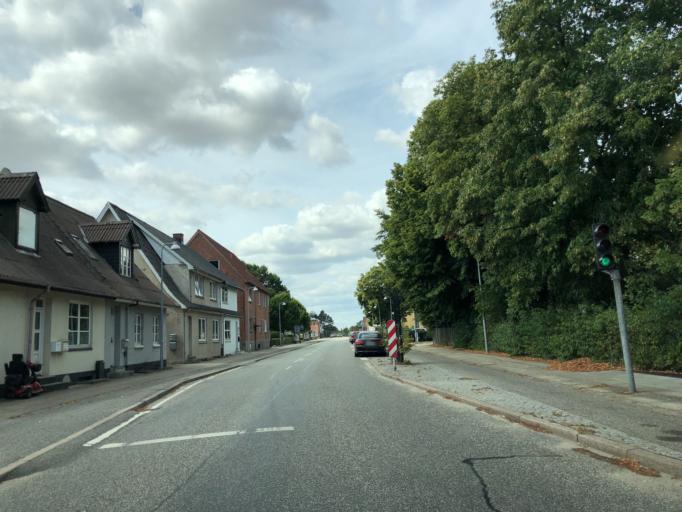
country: DK
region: Central Jutland
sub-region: Herning Kommune
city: Herning
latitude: 56.1359
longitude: 8.9554
